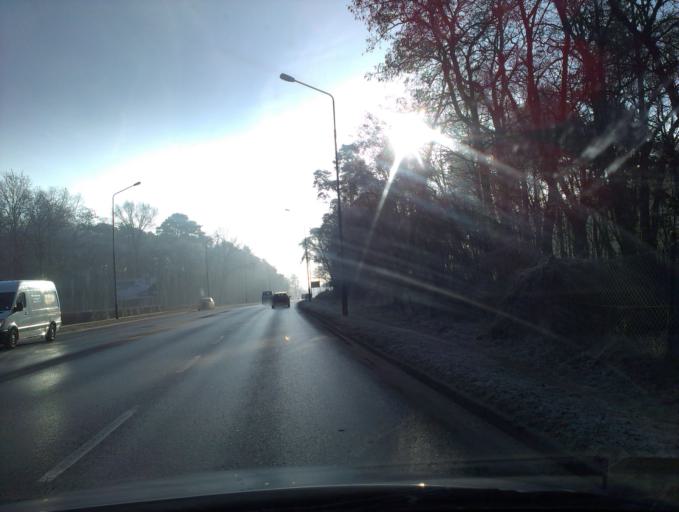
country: PL
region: Greater Poland Voivodeship
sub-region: Poznan
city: Poznan
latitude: 52.3975
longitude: 16.9785
